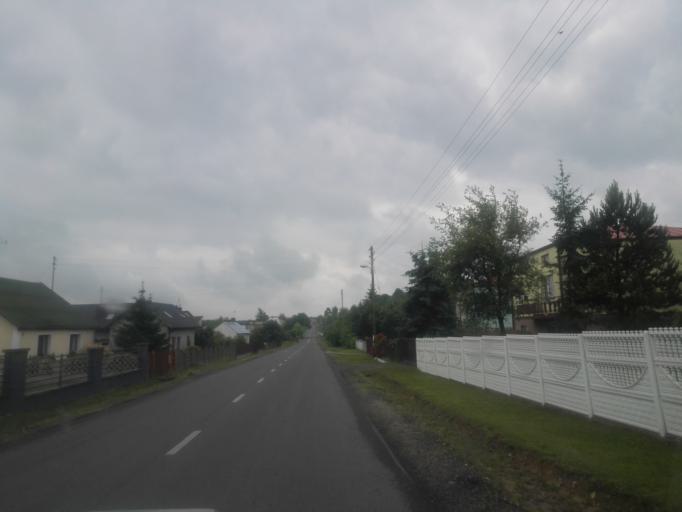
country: PL
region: Silesian Voivodeship
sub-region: Powiat czestochowski
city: Olsztyn
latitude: 50.7334
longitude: 19.3313
